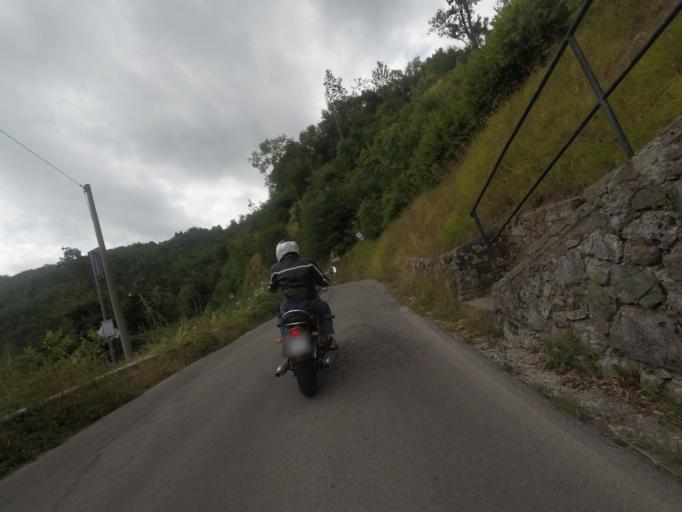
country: IT
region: Tuscany
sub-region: Provincia di Lucca
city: Careggine
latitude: 44.1131
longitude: 10.3647
